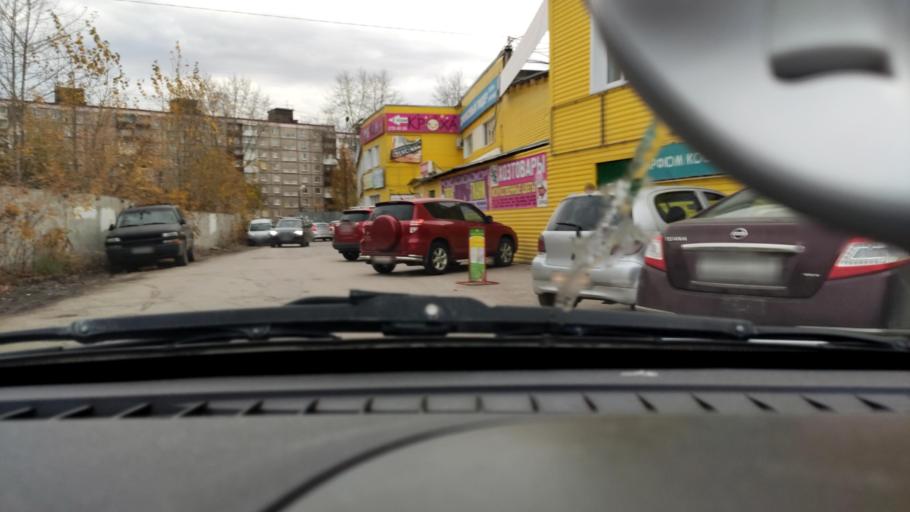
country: RU
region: Perm
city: Kondratovo
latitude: 58.0002
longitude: 56.1615
